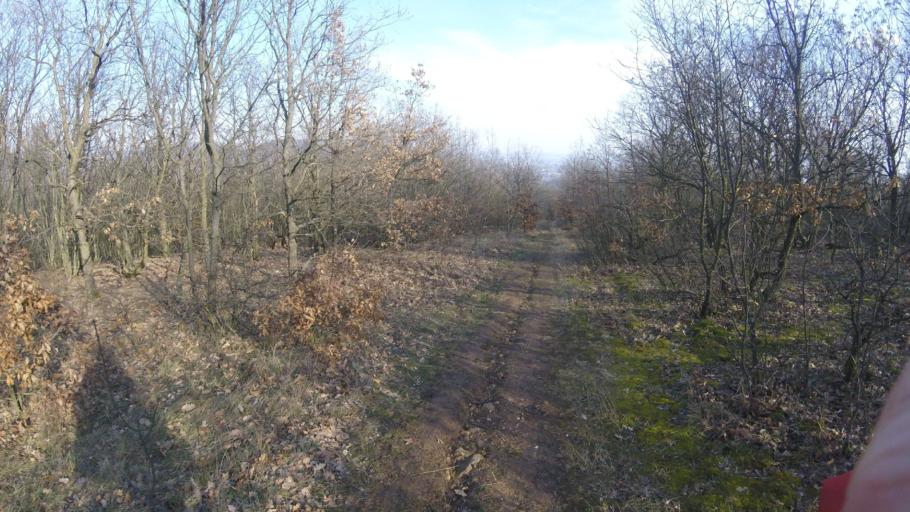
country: HU
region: Pest
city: Csobanka
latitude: 47.6493
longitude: 18.9821
